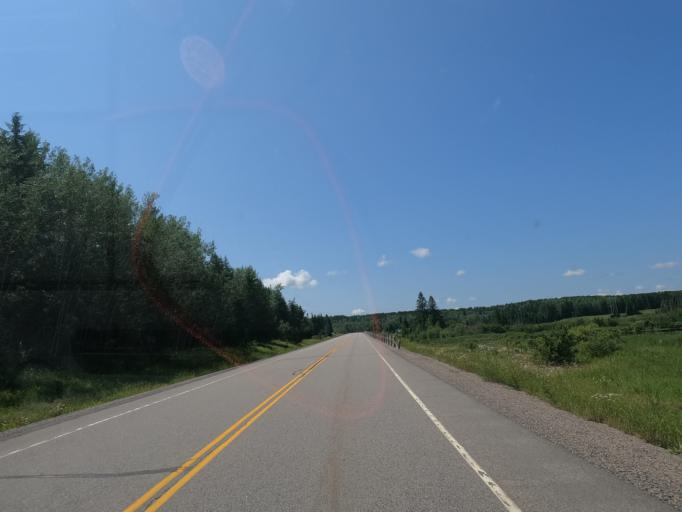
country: CA
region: Ontario
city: Dryden
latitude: 49.8635
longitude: -93.3605
